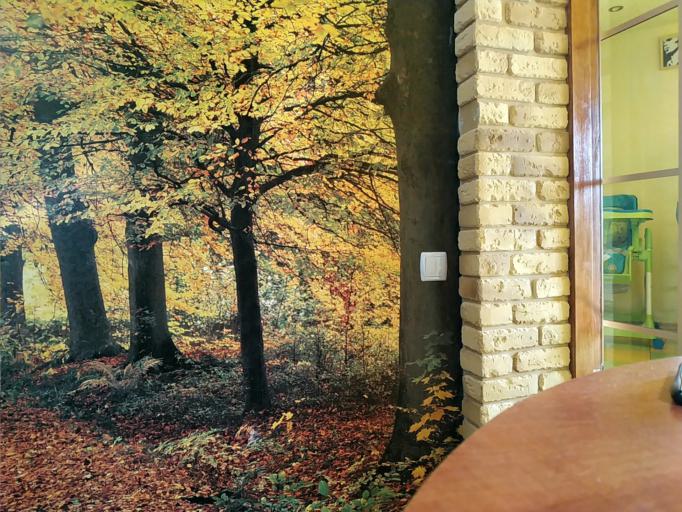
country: RU
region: Novgorod
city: Parfino
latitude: 57.8021
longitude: 31.6057
